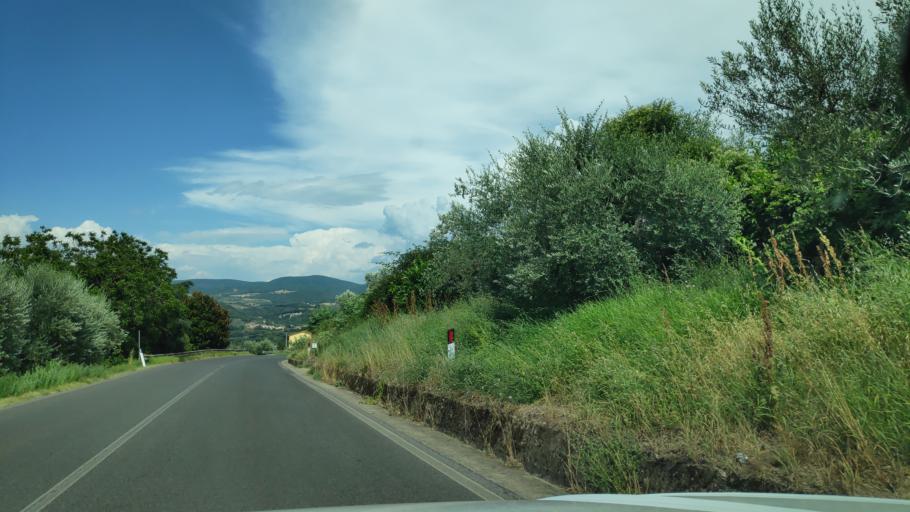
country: IT
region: Umbria
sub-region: Provincia di Terni
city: Orvieto
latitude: 42.7245
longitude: 12.1109
